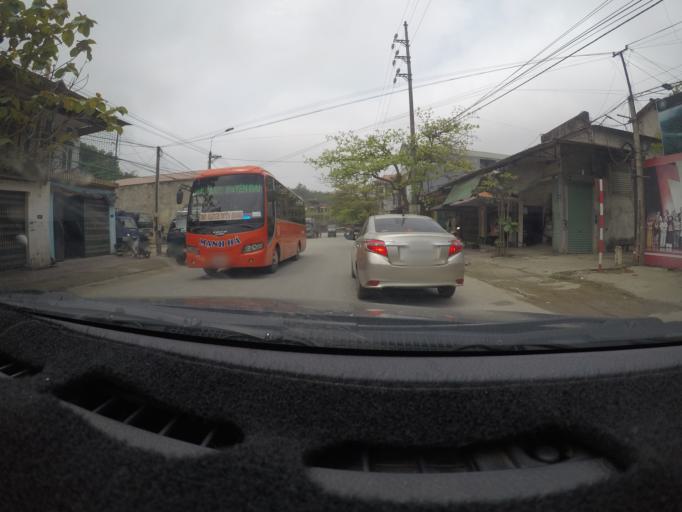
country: VN
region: Yen Bai
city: Yen Bai
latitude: 21.7392
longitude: 104.9487
